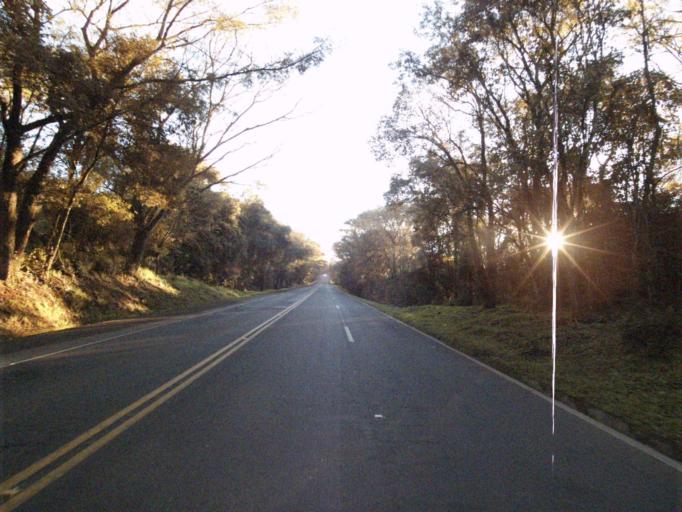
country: BR
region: Santa Catarina
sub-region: Sao Lourenco Do Oeste
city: Sao Lourenco dOeste
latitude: -26.8262
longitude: -53.0515
